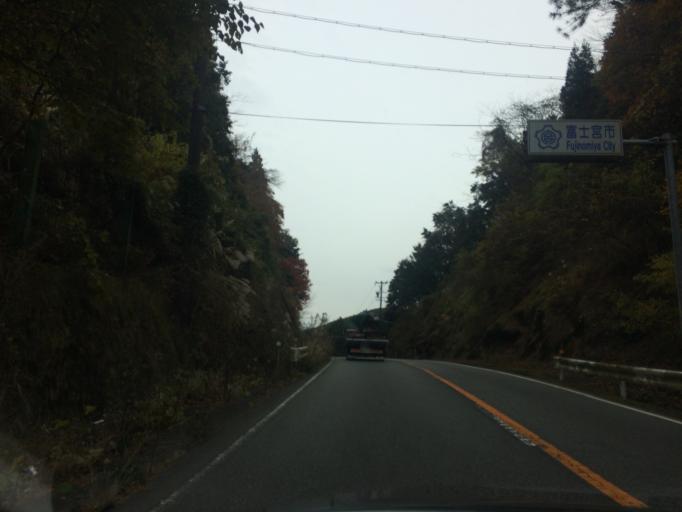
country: JP
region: Shizuoka
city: Fujinomiya
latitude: 35.1792
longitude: 138.5231
